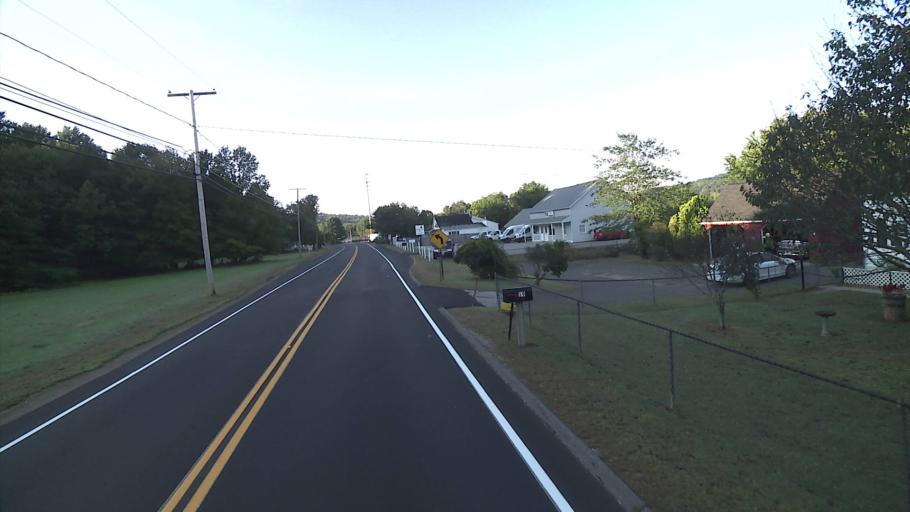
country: US
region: Connecticut
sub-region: Tolland County
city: Storrs
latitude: 41.8391
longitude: -72.3077
